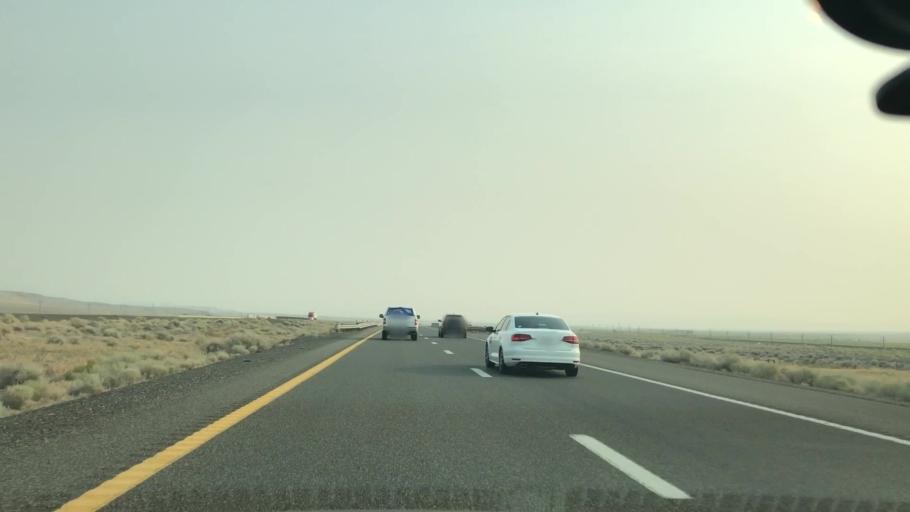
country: US
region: Nevada
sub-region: Pershing County
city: Lovelock
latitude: 40.0094
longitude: -118.6778
